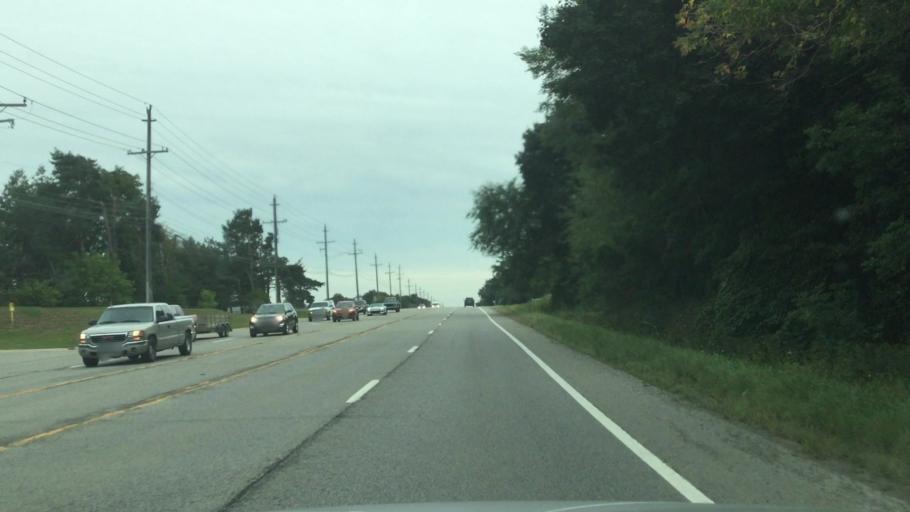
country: US
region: Michigan
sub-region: Oakland County
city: Clarkston
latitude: 42.7469
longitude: -83.4681
